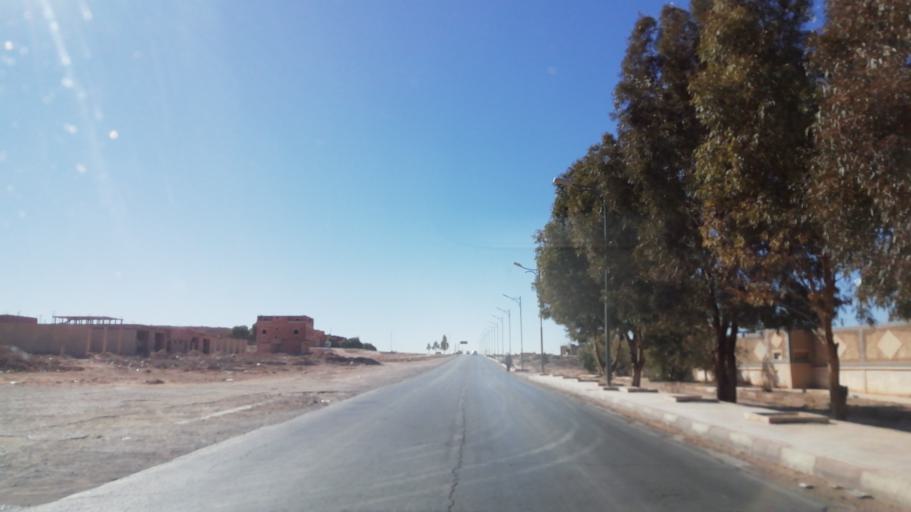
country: DZ
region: Saida
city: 'Ain el Hadjar
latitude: 34.0381
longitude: 0.0795
